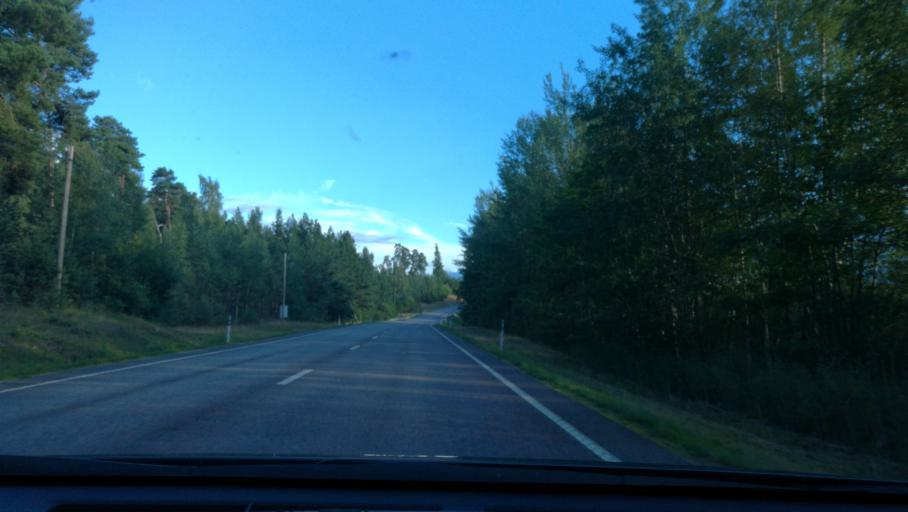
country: SE
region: Vaestmanland
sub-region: Kungsors Kommun
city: Kungsoer
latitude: 59.2670
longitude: 16.1186
